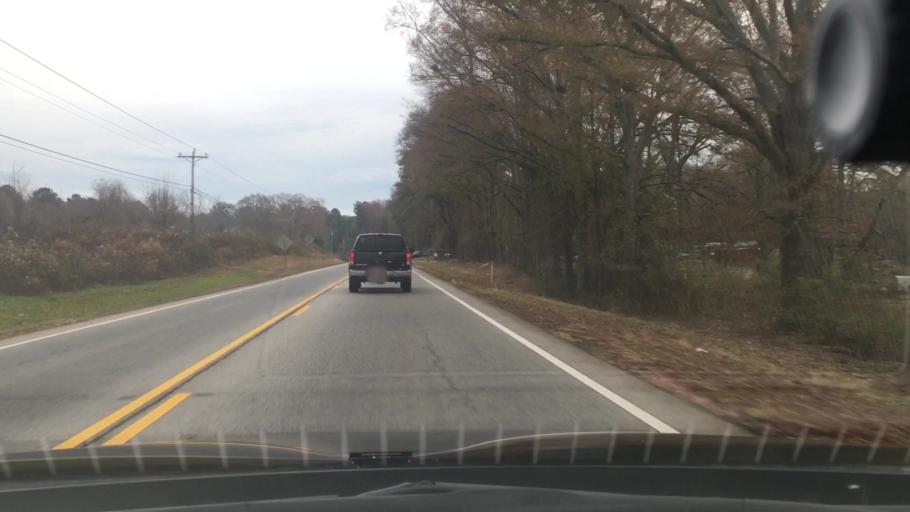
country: US
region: Georgia
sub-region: Spalding County
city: Experiment
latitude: 33.2391
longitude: -84.4015
